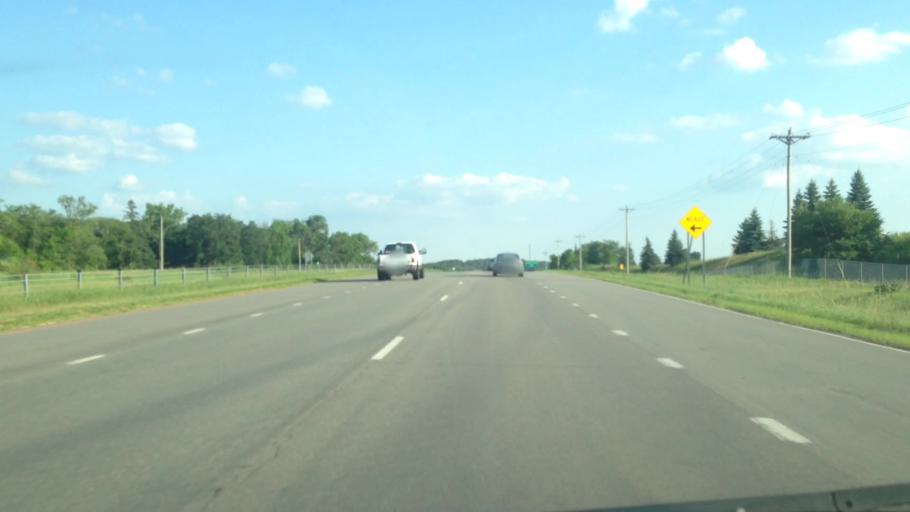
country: US
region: Minnesota
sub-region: Sherburne County
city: Zimmerman
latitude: 45.3766
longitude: -93.5640
